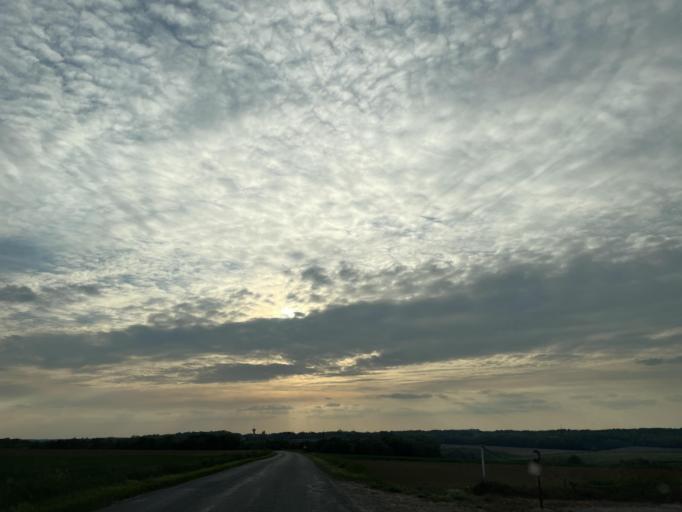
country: FR
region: Ile-de-France
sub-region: Departement de Seine-et-Marne
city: Bouleurs
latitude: 48.8936
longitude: 2.9172
